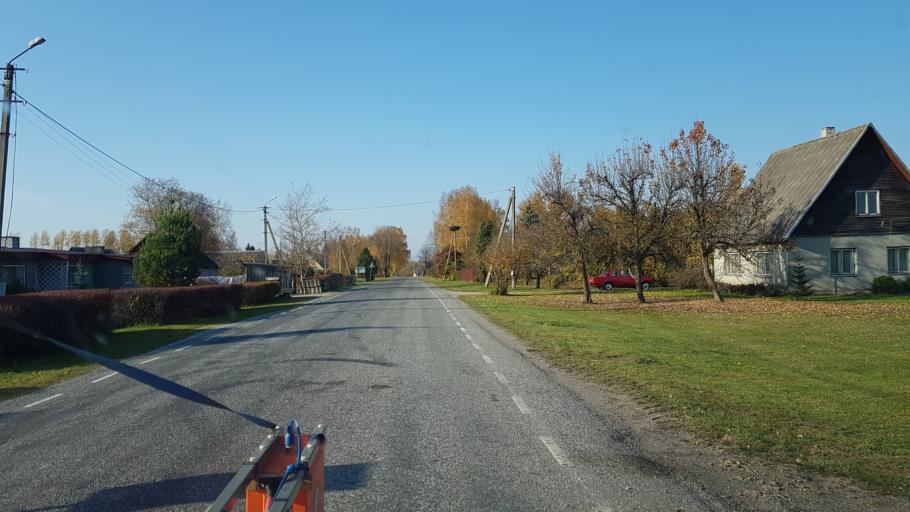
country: EE
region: Vorumaa
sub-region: Antsla vald
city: Vana-Antsla
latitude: 57.8423
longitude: 26.4774
